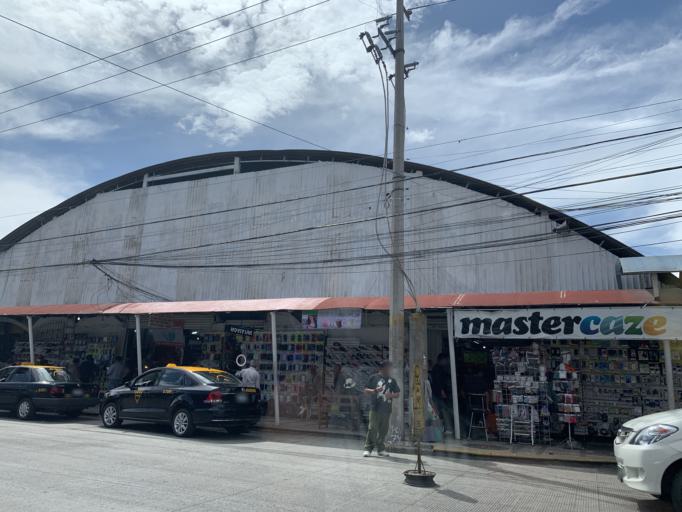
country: MX
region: Puebla
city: Puebla
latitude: 19.0720
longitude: -98.2057
